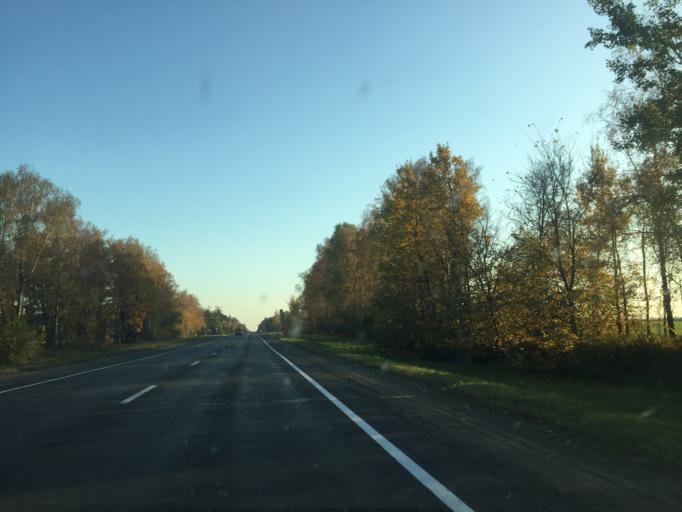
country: BY
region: Mogilev
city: Poselok Voskhod
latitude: 53.7356
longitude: 30.3664
